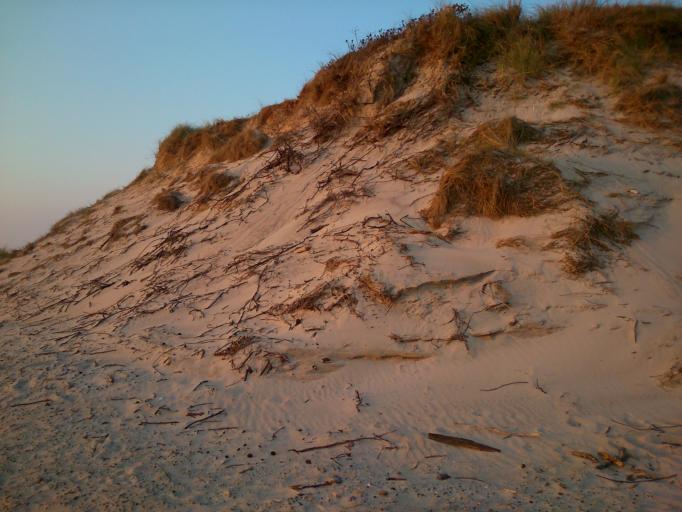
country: DK
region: Central Jutland
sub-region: Ringkobing-Skjern Kommune
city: Hvide Sande
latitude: 55.8805
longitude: 8.1560
